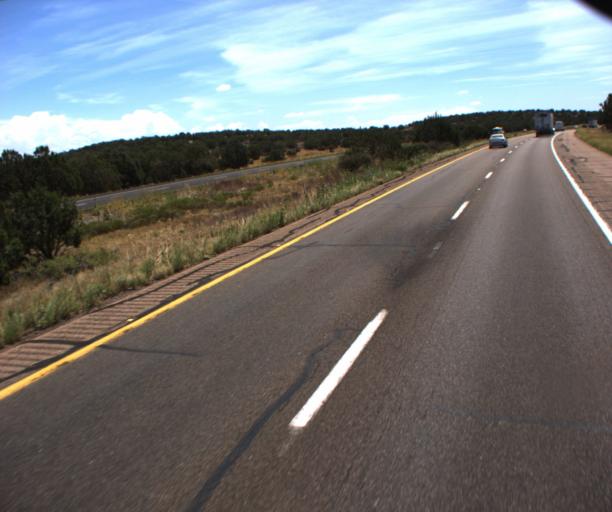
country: US
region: Arizona
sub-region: Yavapai County
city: Paulden
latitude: 35.2700
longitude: -112.7305
